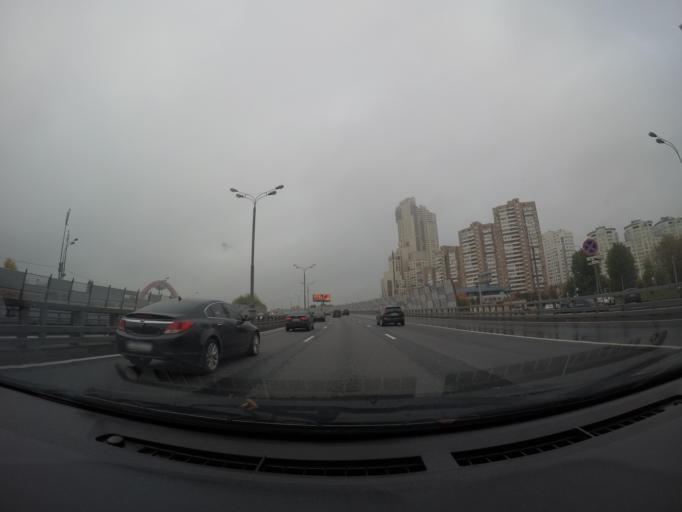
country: RU
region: Moskovskaya
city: Khoroshevo-Mnevniki
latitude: 55.7787
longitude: 37.4554
